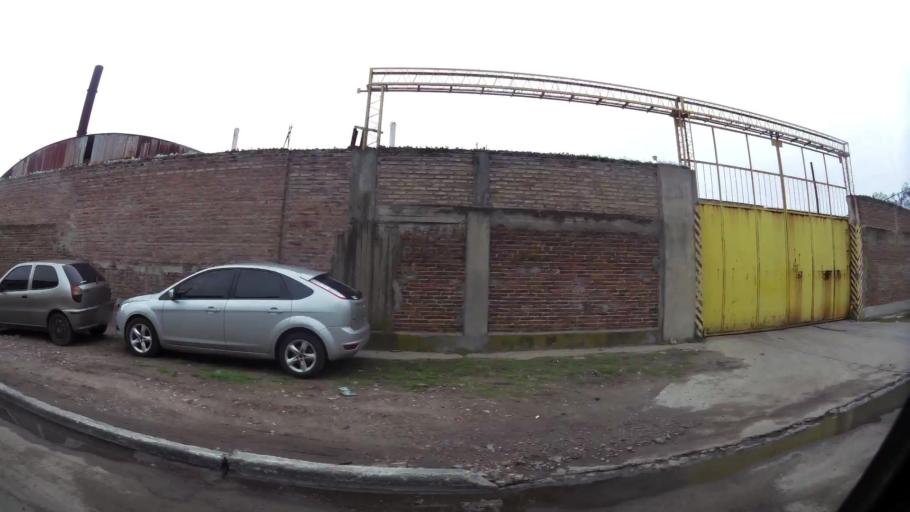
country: AR
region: Buenos Aires
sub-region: Partido de Lanus
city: Lanus
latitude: -34.7102
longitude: -58.3625
